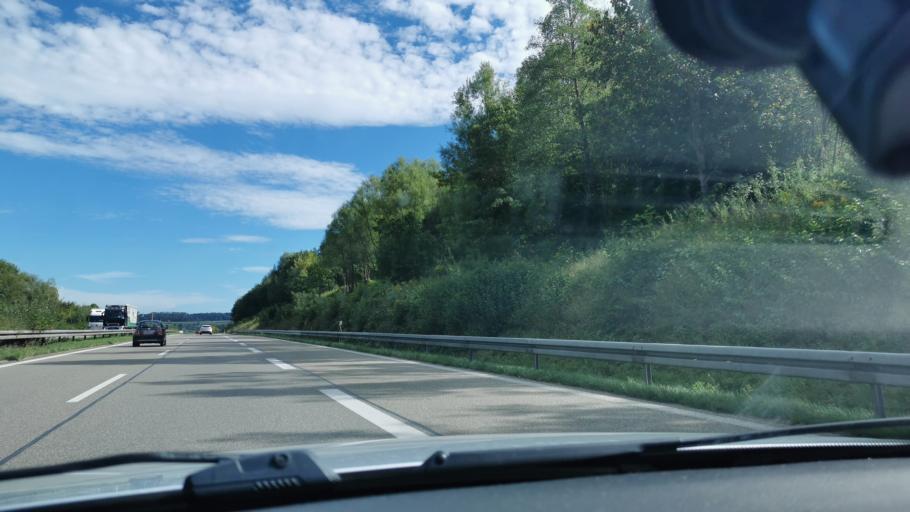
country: DE
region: Baden-Wuerttemberg
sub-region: Regierungsbezirk Stuttgart
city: Albershausen
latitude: 48.7126
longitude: 9.5609
